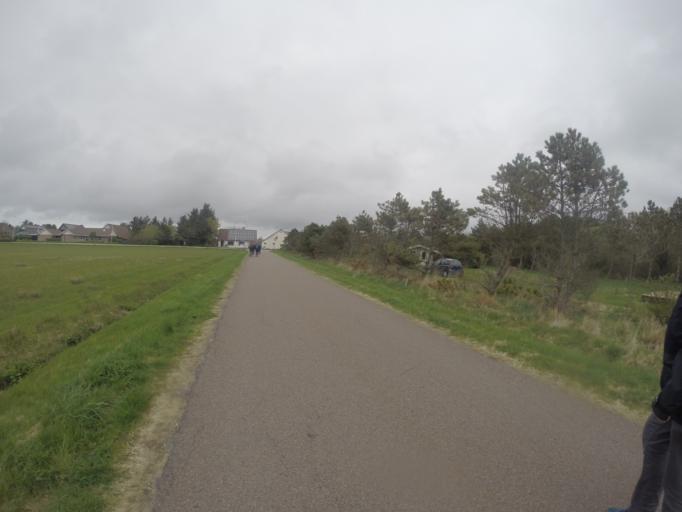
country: DK
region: North Denmark
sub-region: Thisted Kommune
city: Hurup
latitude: 56.9189
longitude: 8.3604
